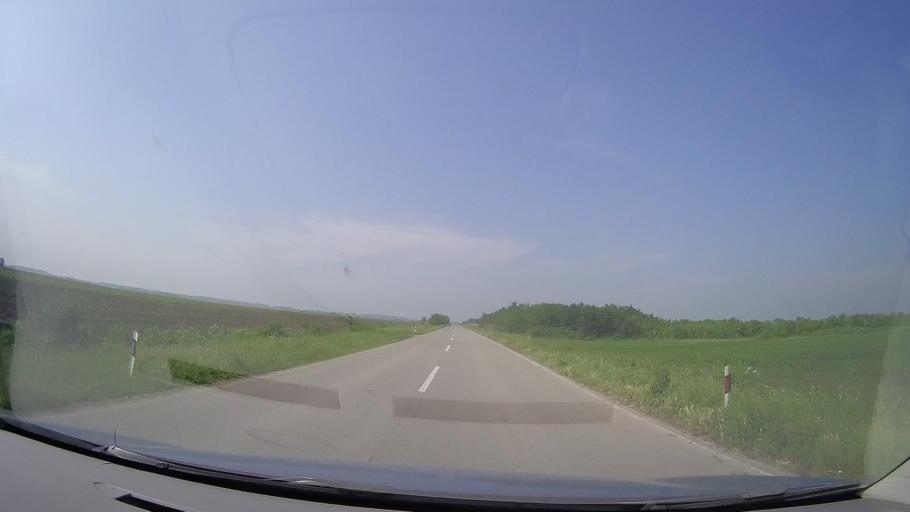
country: RS
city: Boka
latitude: 45.3971
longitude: 20.8097
